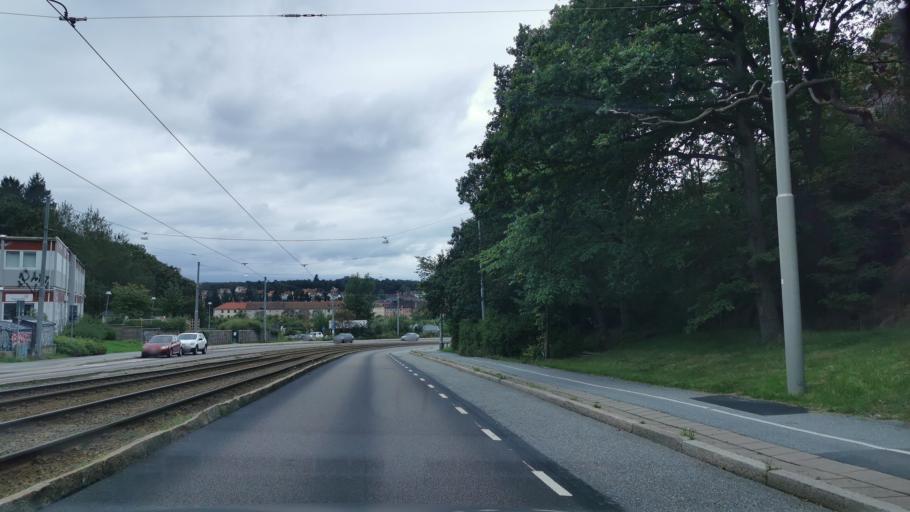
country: SE
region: Vaestra Goetaland
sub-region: Goteborg
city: Majorna
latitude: 57.6883
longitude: 11.9329
